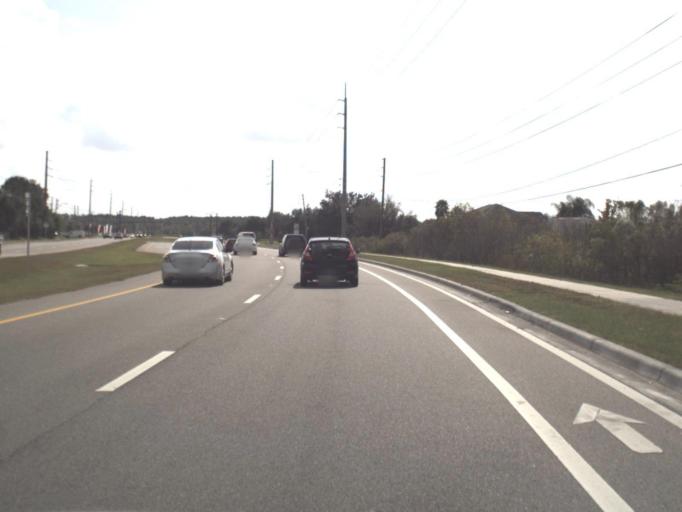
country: US
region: Florida
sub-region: Osceola County
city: Campbell
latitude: 28.2288
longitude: -81.4873
